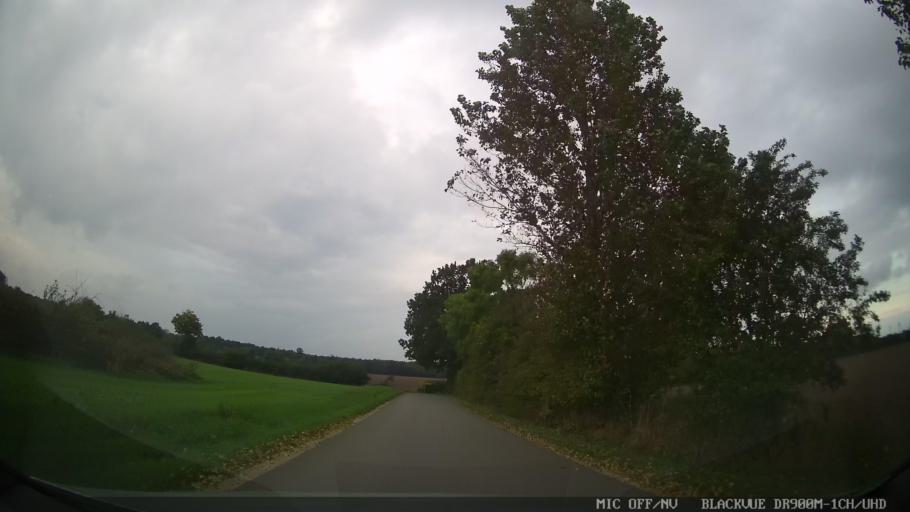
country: DE
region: Schleswig-Holstein
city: Manhagen
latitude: 54.1845
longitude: 10.9504
